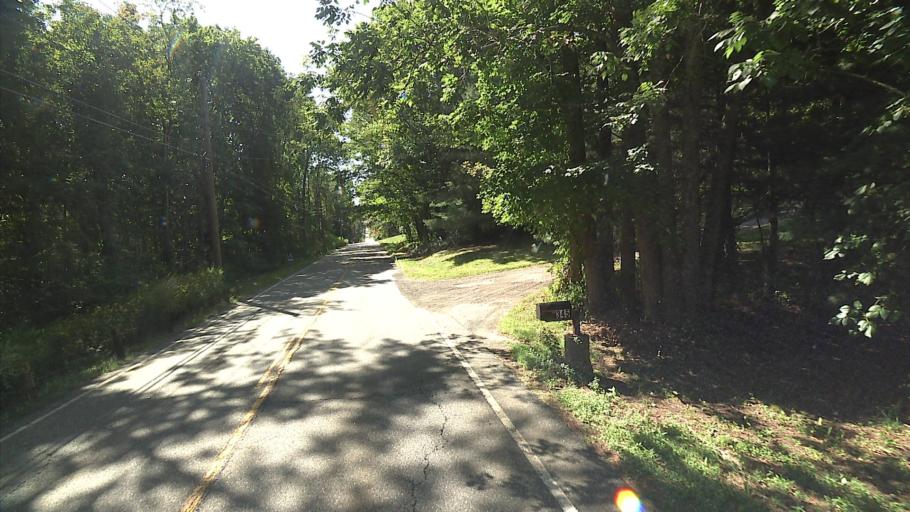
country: US
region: Connecticut
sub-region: Litchfield County
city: Northwest Harwinton
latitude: 41.7446
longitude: -73.0790
